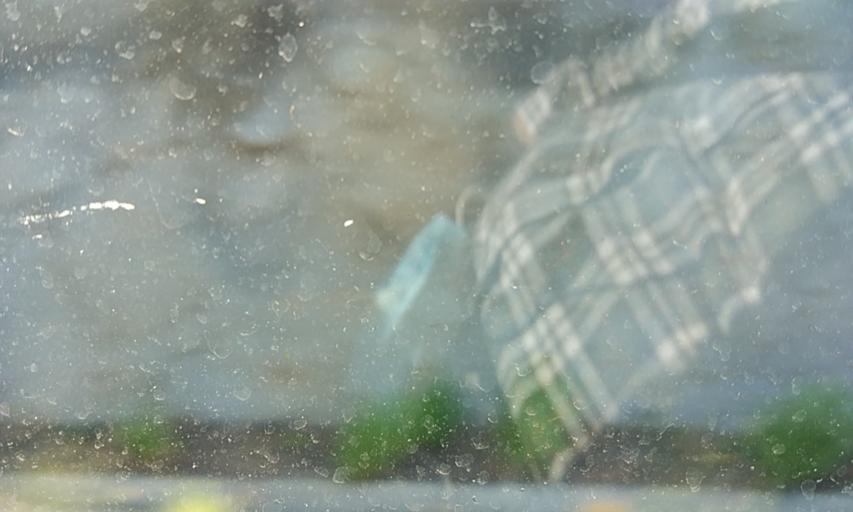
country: PT
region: Vila Real
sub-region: Murca
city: Murca
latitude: 41.4084
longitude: -7.4230
